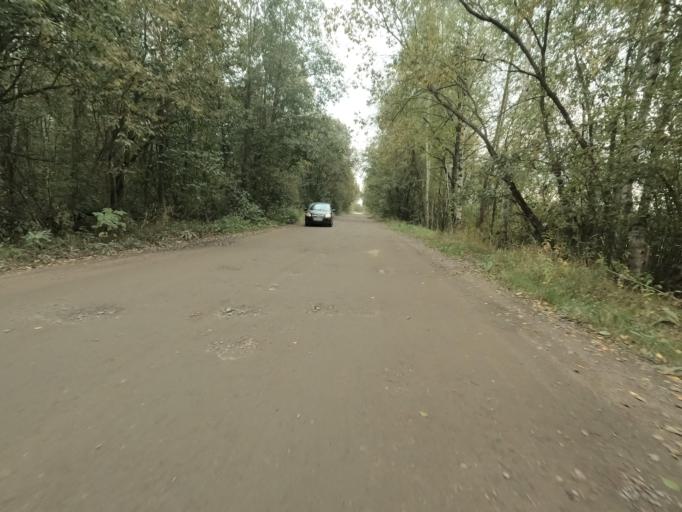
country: RU
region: St.-Petersburg
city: Sapernyy
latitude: 59.7608
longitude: 30.6532
